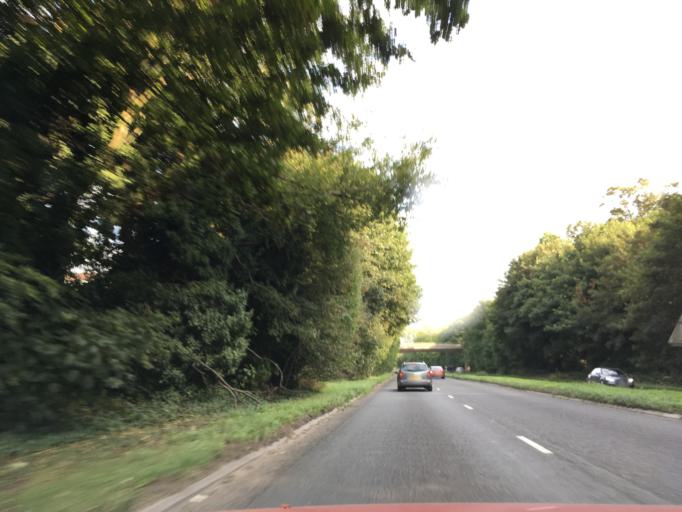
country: GB
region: England
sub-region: Gloucestershire
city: Cirencester
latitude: 51.7120
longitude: -1.9708
